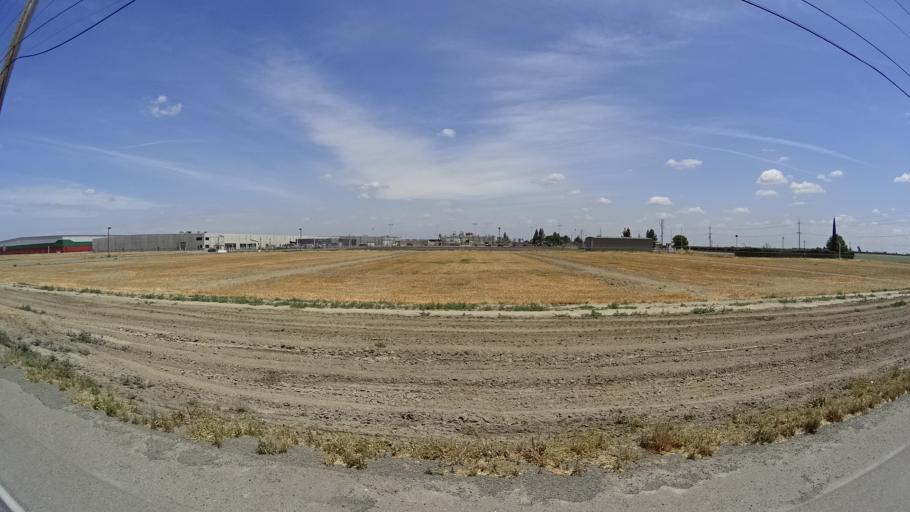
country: US
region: California
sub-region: Kings County
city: Home Garden
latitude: 36.2561
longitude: -119.6549
